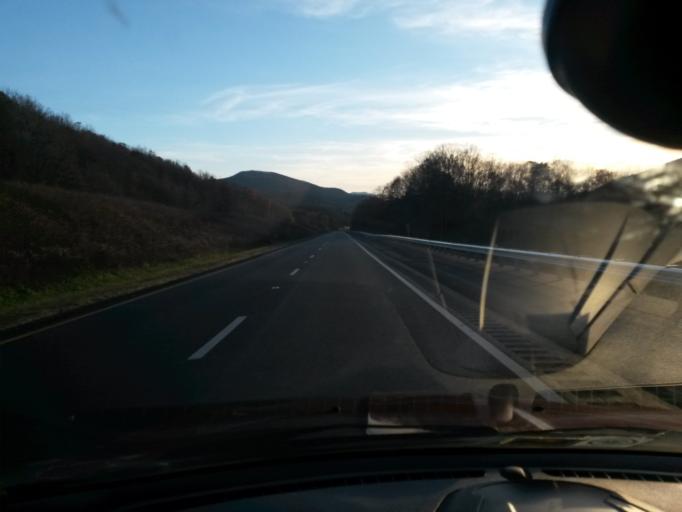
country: US
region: Virginia
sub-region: City of Lexington
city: Lexington
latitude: 37.8570
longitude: -79.6279
